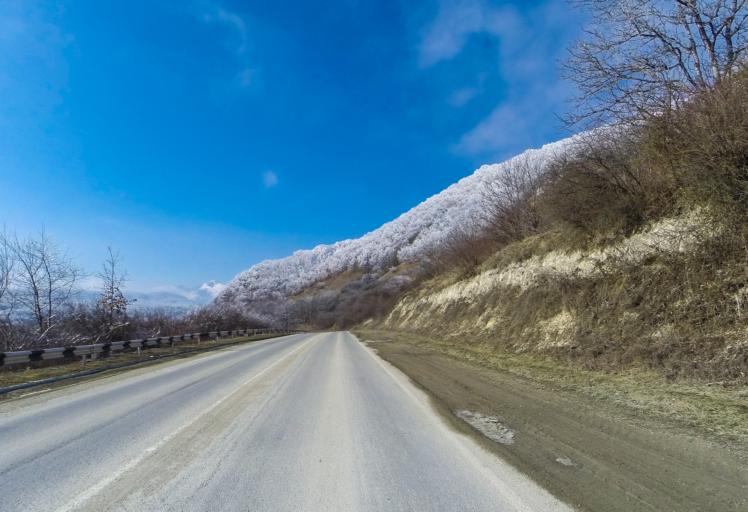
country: RU
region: Kabardino-Balkariya
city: Kashkhatau
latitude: 43.3340
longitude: 43.6499
